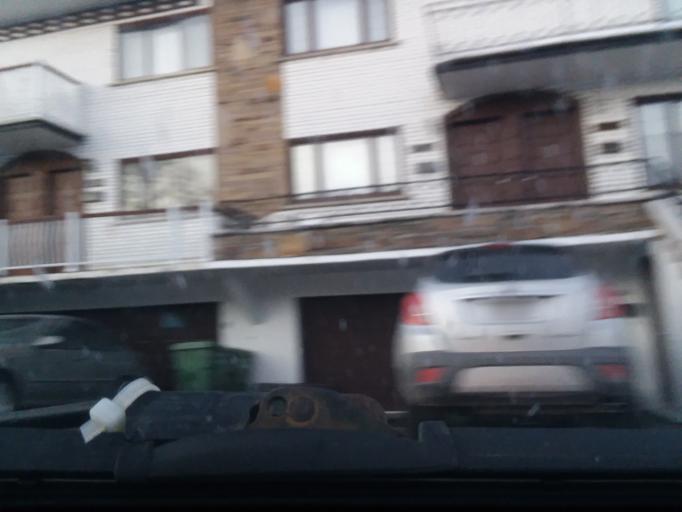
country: CA
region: Quebec
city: Montreal-Ouest
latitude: 45.4387
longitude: -73.6321
